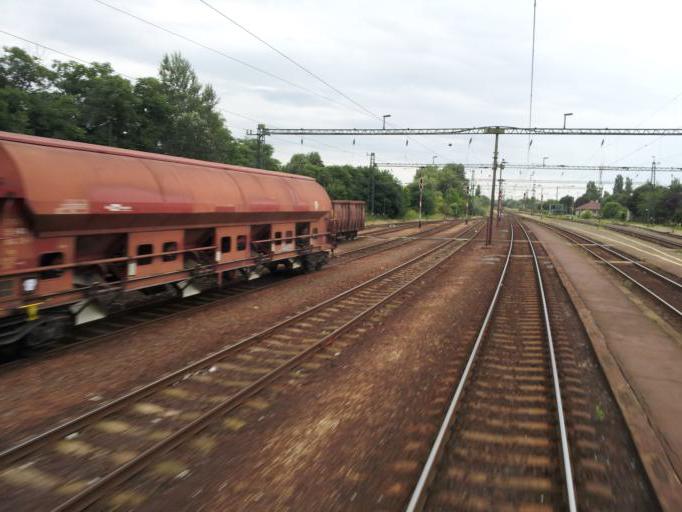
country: HU
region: Fejer
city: Szabadbattyan
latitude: 47.1056
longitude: 18.3887
